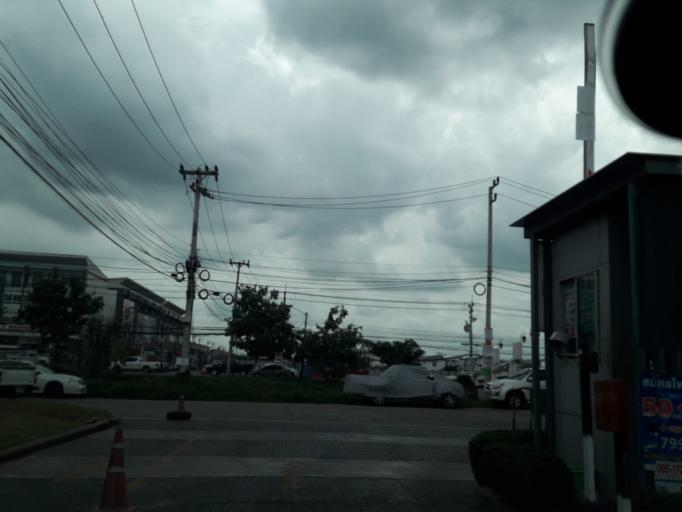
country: TH
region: Pathum Thani
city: Khlong Luang
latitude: 14.0459
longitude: 100.6643
